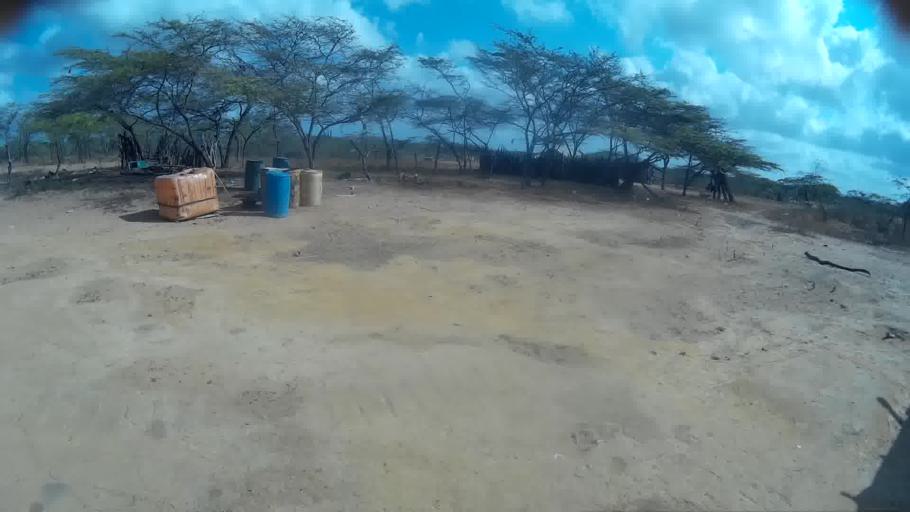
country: CO
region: La Guajira
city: Maicao
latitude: 11.3962
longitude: -72.2240
